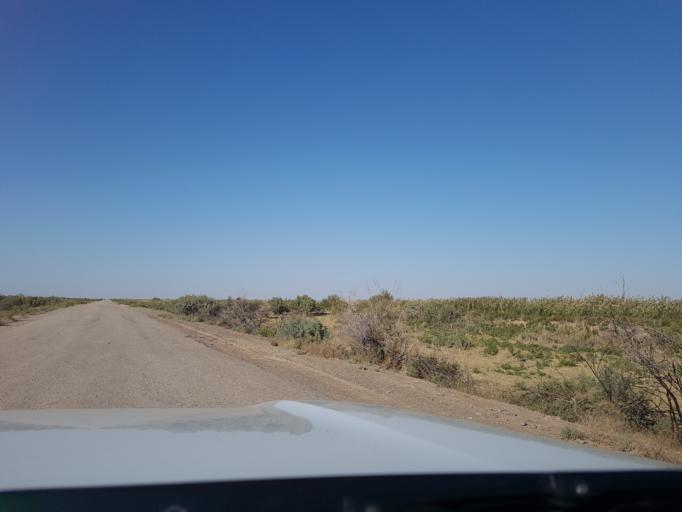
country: IR
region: Razavi Khorasan
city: Sarakhs
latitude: 36.9605
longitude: 61.3820
